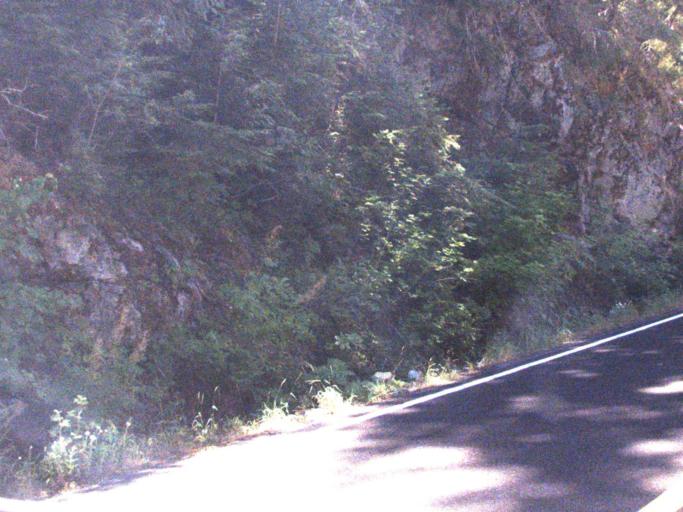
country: US
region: Washington
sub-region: King County
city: Enumclaw
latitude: 46.8244
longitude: -121.5456
